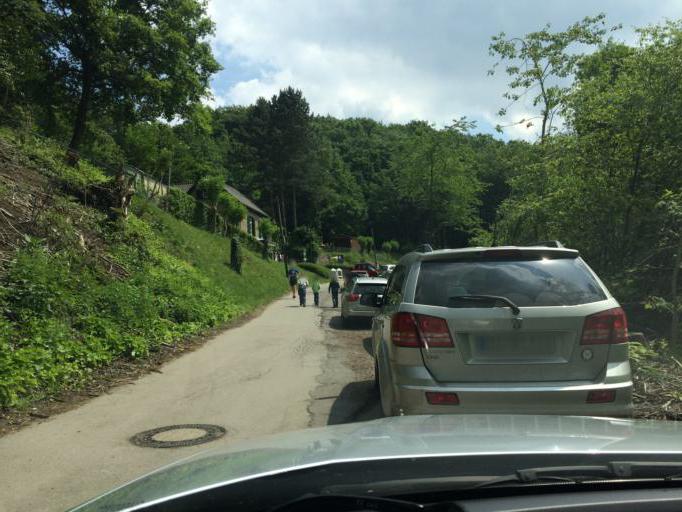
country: DE
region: North Rhine-Westphalia
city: Witten
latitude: 51.4238
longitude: 7.3174
